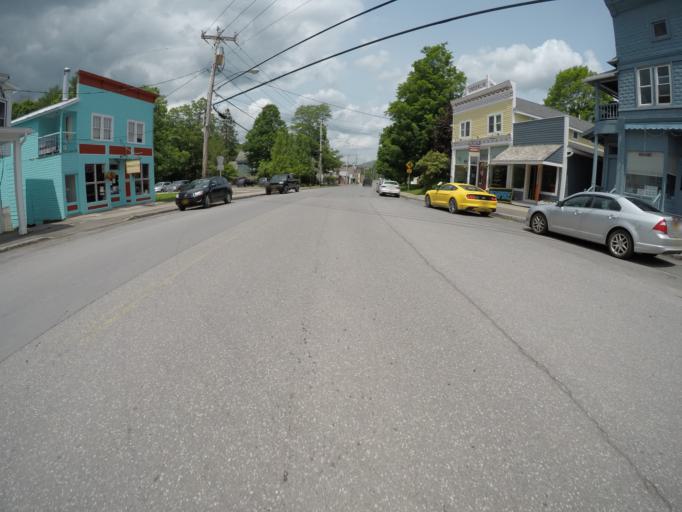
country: US
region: New York
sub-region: Delaware County
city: Stamford
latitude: 42.2839
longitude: -74.5650
